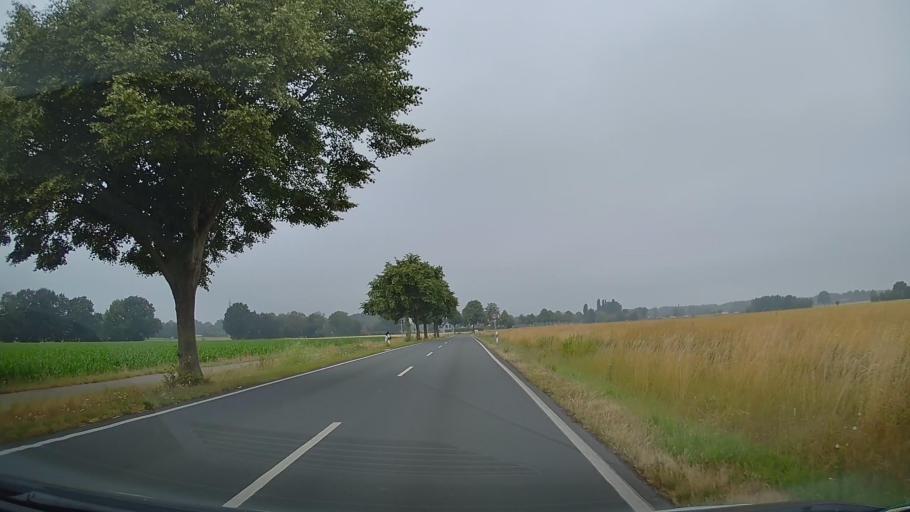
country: DE
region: North Rhine-Westphalia
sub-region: Regierungsbezirk Detmold
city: Minden
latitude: 52.3552
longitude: 8.8442
